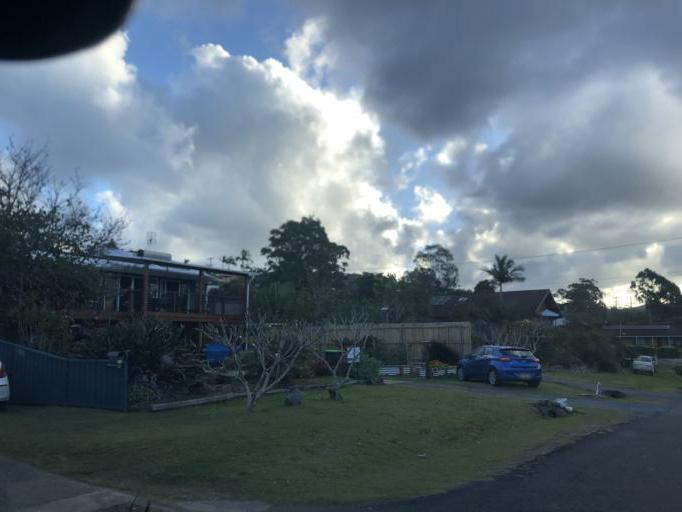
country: AU
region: New South Wales
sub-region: Coffs Harbour
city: Woolgoolga
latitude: -30.0967
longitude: 153.1949
